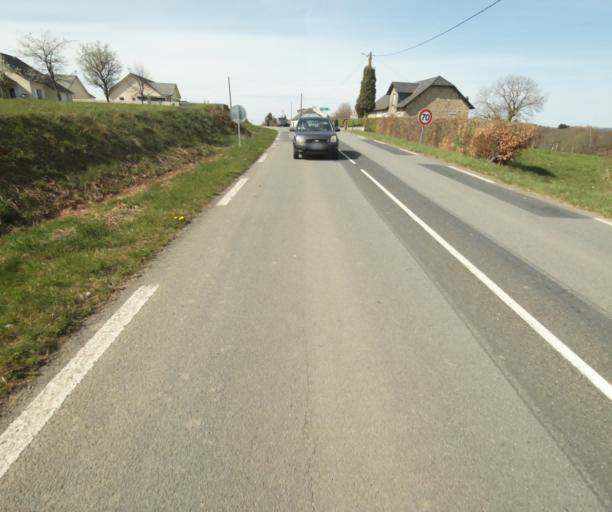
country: FR
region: Limousin
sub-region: Departement de la Correze
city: Seilhac
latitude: 45.3602
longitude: 1.7265
